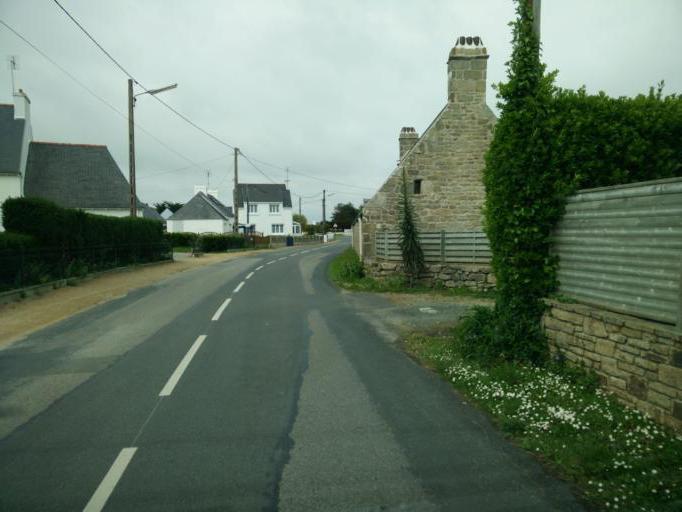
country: FR
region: Brittany
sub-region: Departement du Finistere
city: Loctudy
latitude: 47.8071
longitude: -4.1846
